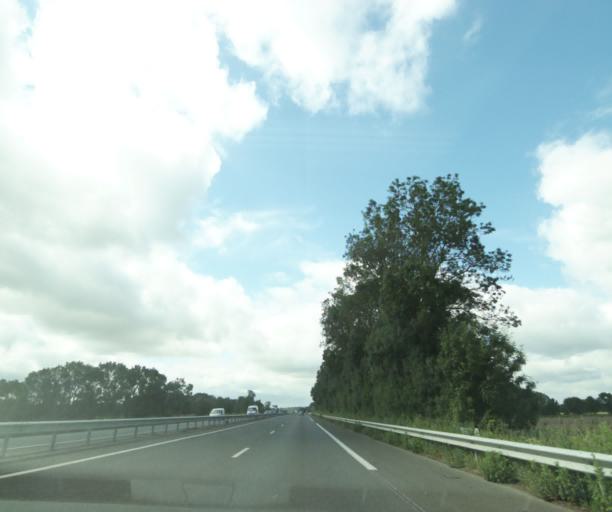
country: FR
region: Pays de la Loire
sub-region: Departement de Maine-et-Loire
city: Vivy
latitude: 47.2954
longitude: -0.0408
